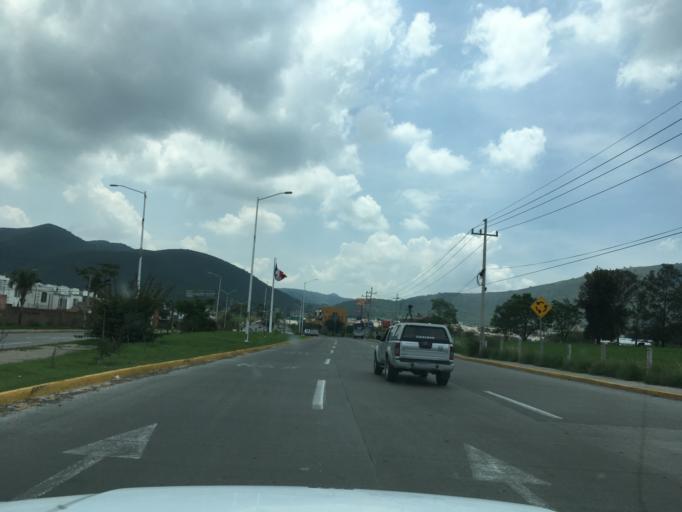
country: MX
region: Jalisco
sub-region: Tlajomulco de Zuniga
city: Santa Cruz de las Flores
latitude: 20.4903
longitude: -103.4891
